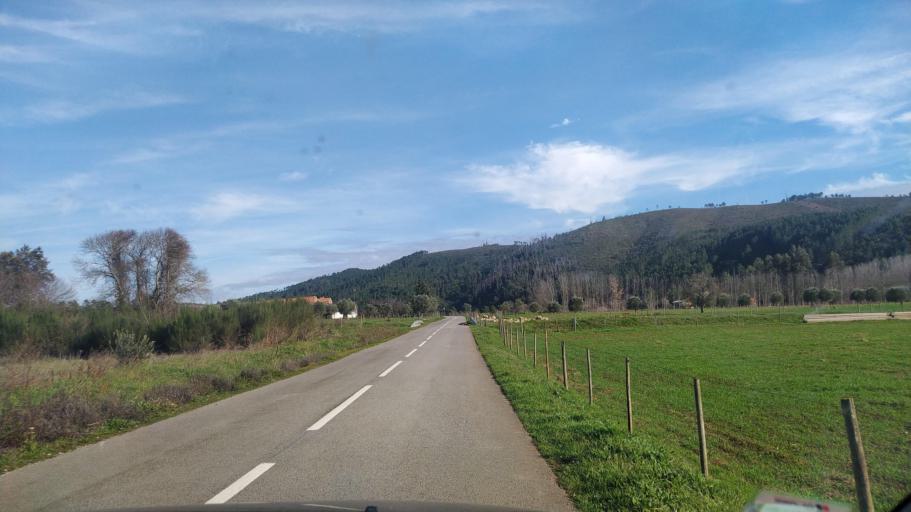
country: PT
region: Castelo Branco
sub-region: Concelho do Fundao
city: Aldeia de Joanes
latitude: 40.1797
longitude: -7.6542
